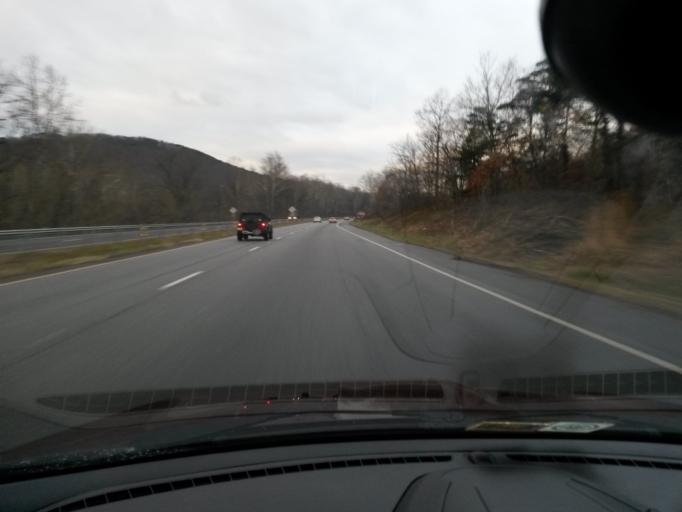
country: US
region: Virginia
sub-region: Alleghany County
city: Clifton Forge
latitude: 37.8064
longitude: -79.8542
